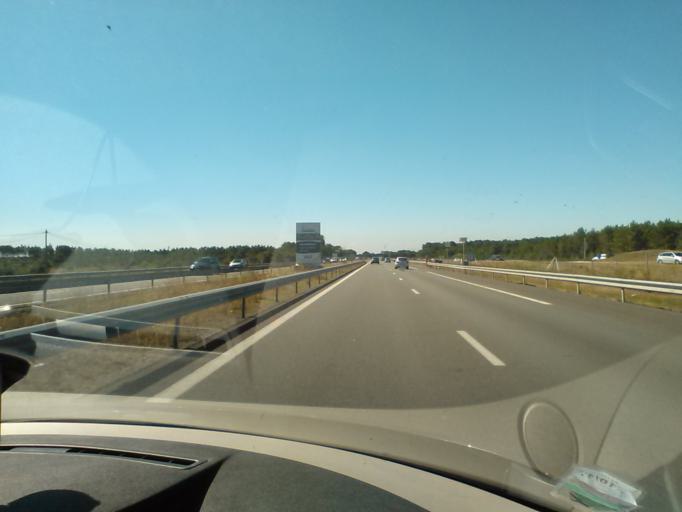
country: FR
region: Aquitaine
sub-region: Departement des Landes
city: Saint-Geours-de-Maremne
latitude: 43.7069
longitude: -1.2284
